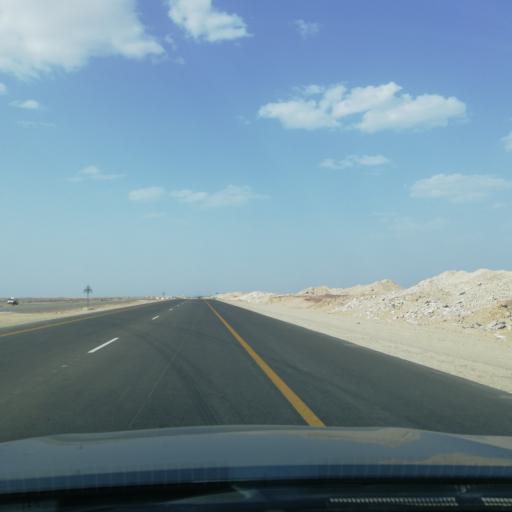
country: OM
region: Muhafazat ad Dakhiliyah
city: Adam
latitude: 22.0276
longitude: 57.5004
